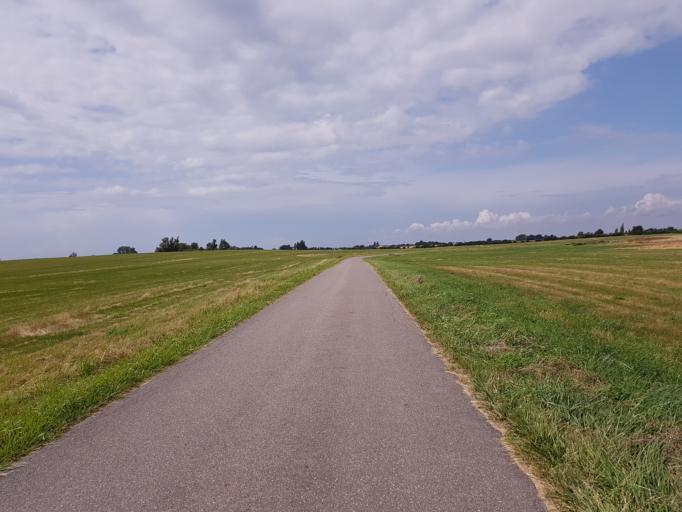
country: DK
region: Zealand
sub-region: Guldborgsund Kommune
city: Nykobing Falster
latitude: 54.5801
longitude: 11.9618
